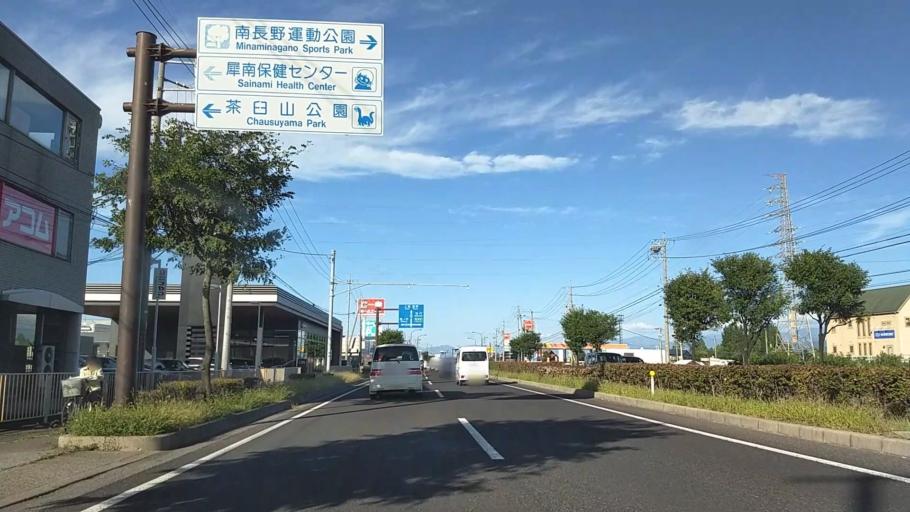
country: JP
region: Nagano
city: Nagano-shi
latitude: 36.5801
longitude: 138.1608
